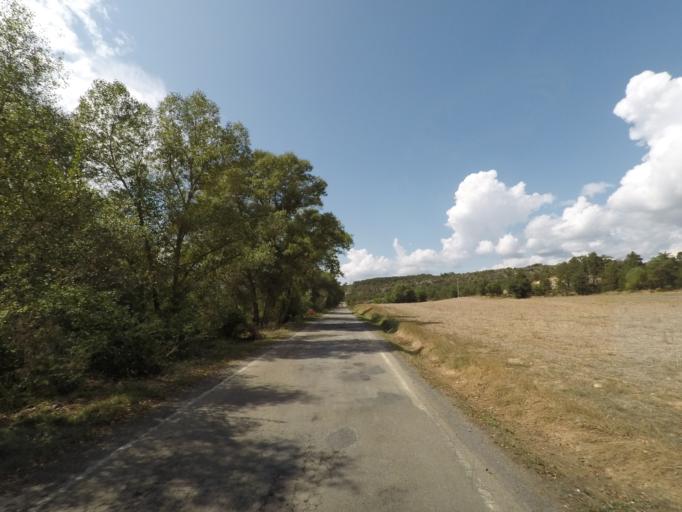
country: ES
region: Aragon
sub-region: Provincia de Huesca
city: Arguis
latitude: 42.4021
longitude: -0.3680
